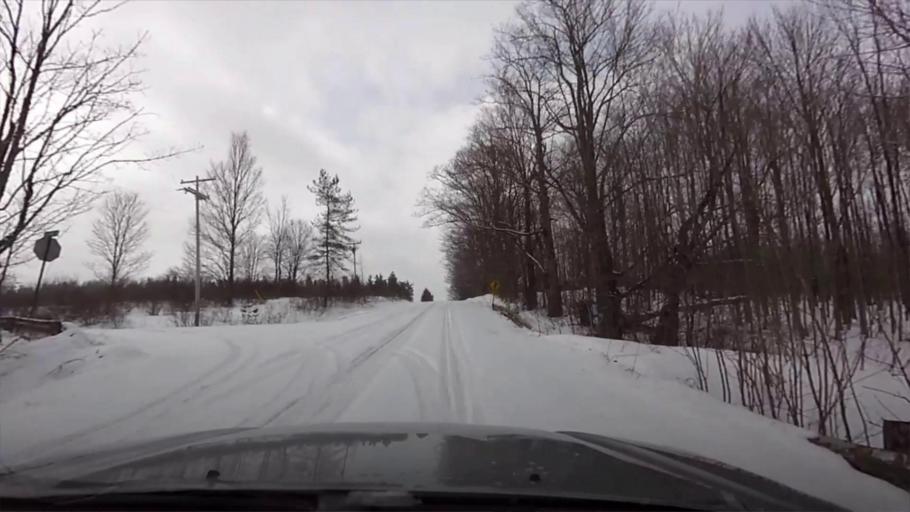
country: US
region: New York
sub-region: Cattaraugus County
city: Franklinville
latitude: 42.3207
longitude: -78.3540
